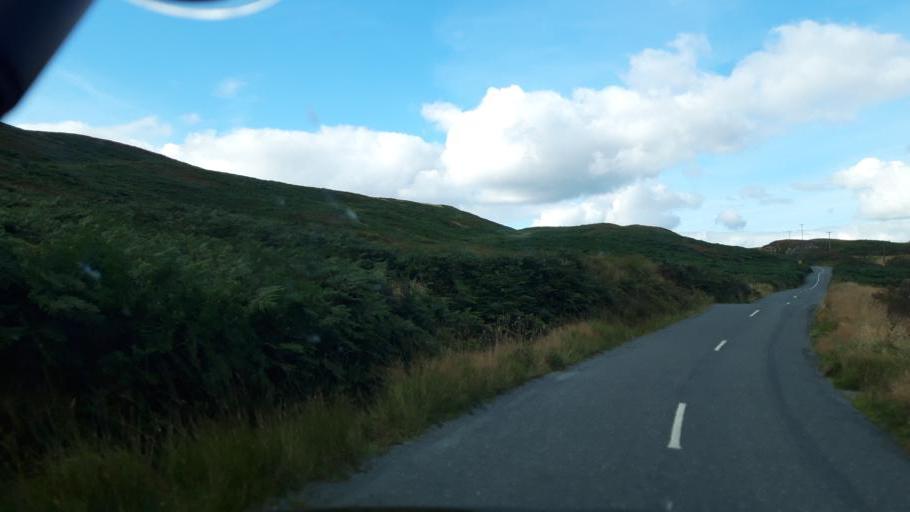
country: GB
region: Northern Ireland
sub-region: Down District
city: Warrenpoint
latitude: 54.0571
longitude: -6.2738
